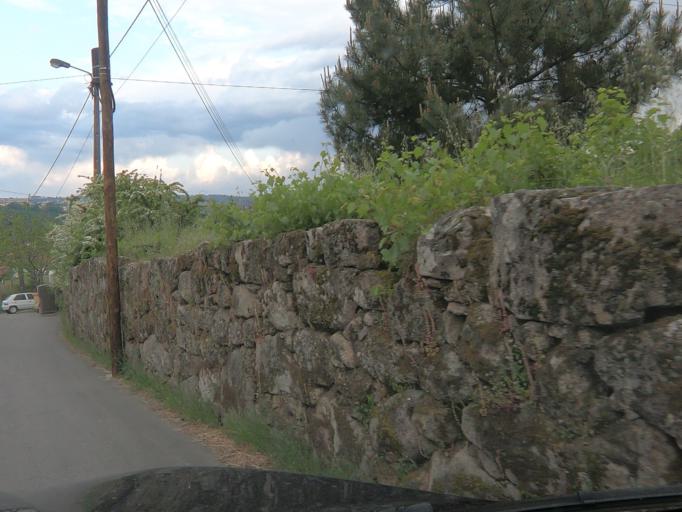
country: PT
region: Vila Real
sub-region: Vila Real
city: Vila Real
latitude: 41.3203
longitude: -7.7619
